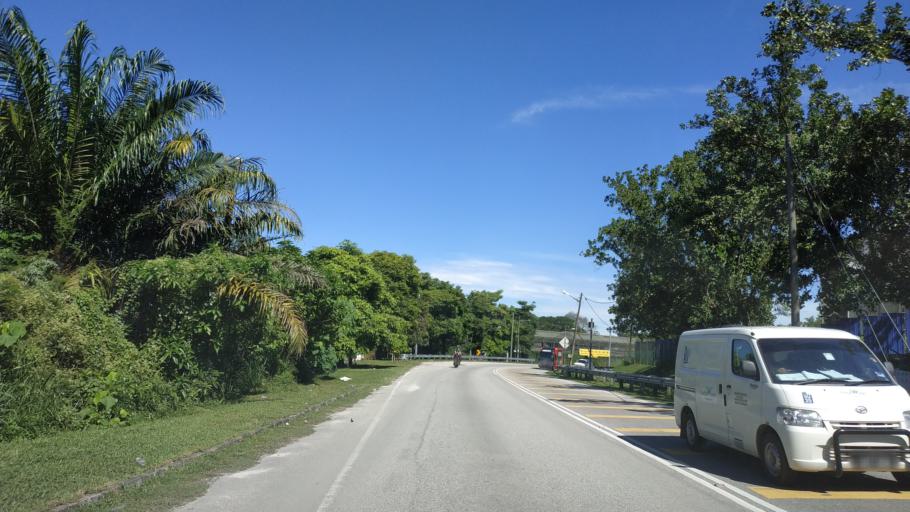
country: MY
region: Kedah
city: Kulim
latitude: 5.3418
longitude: 100.5374
